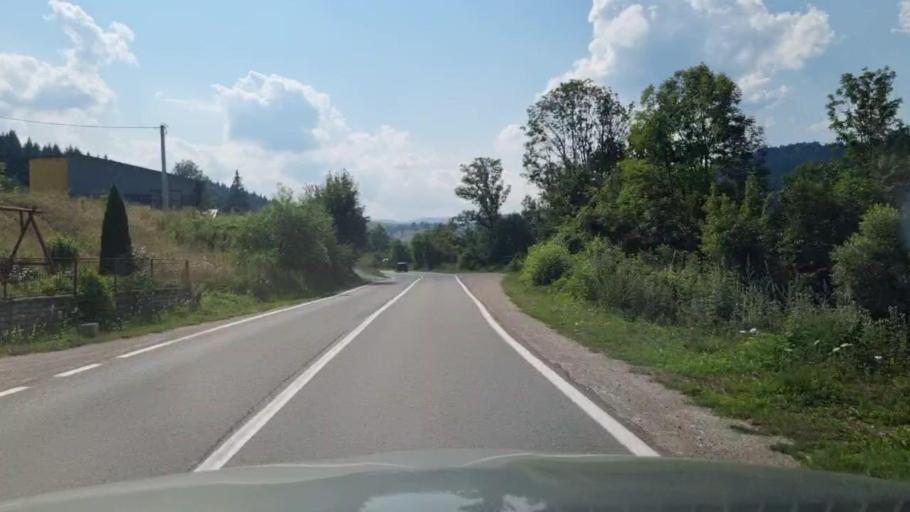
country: BA
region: Federation of Bosnia and Herzegovina
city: Olovo
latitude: 44.1277
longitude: 18.5972
